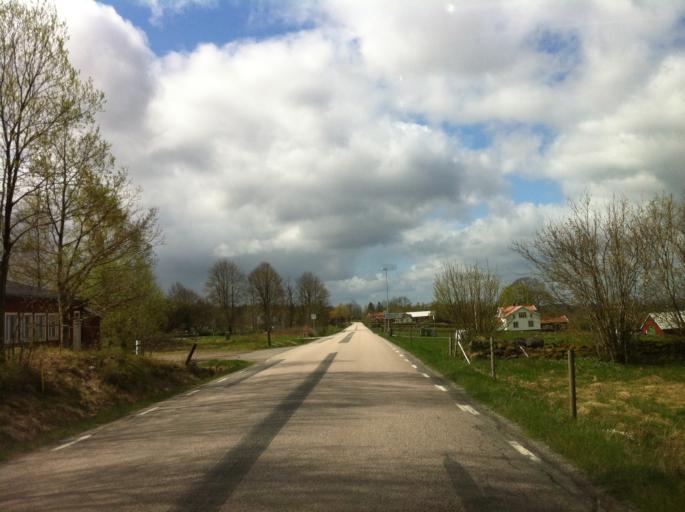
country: SE
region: Vaestra Goetaland
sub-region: Alingsas Kommun
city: Ingared
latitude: 57.8116
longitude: 12.5472
